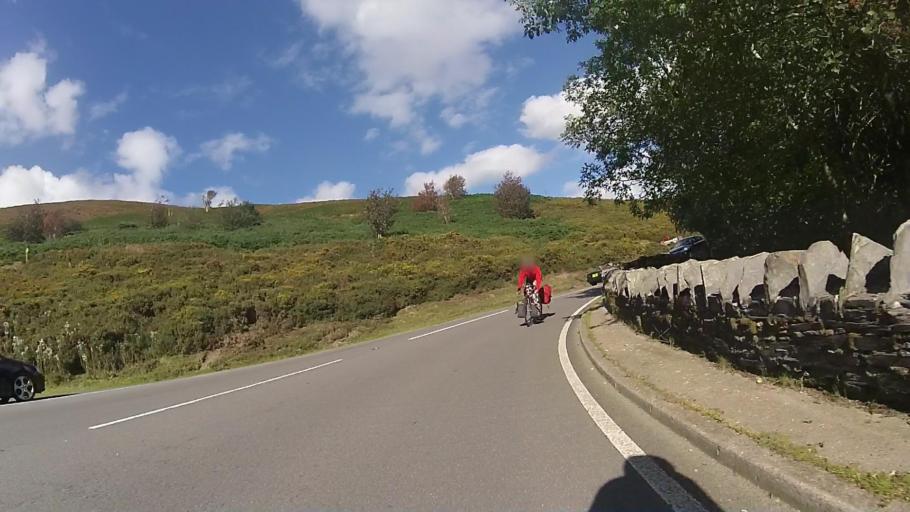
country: GB
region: Wales
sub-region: Denbighshire
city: Llandegla
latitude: 53.0143
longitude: -3.2159
